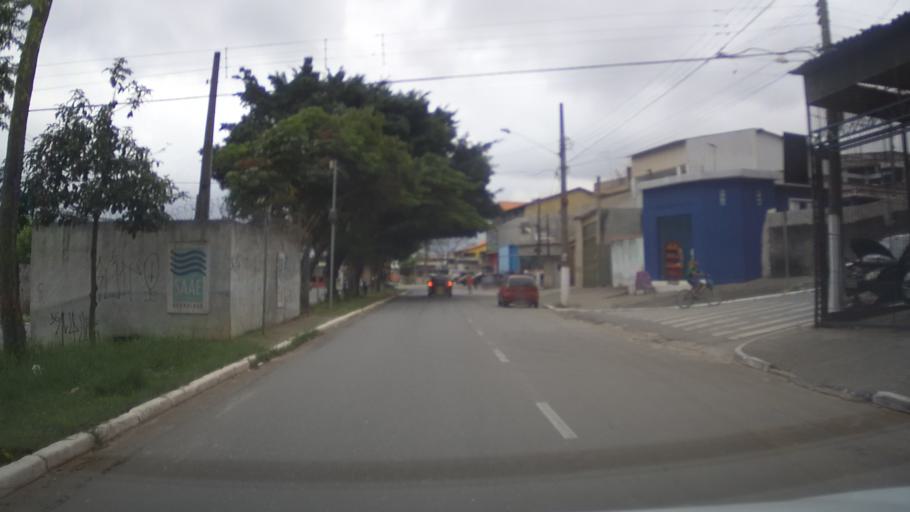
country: BR
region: Sao Paulo
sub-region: Guarulhos
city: Guarulhos
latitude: -23.4116
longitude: -46.4464
